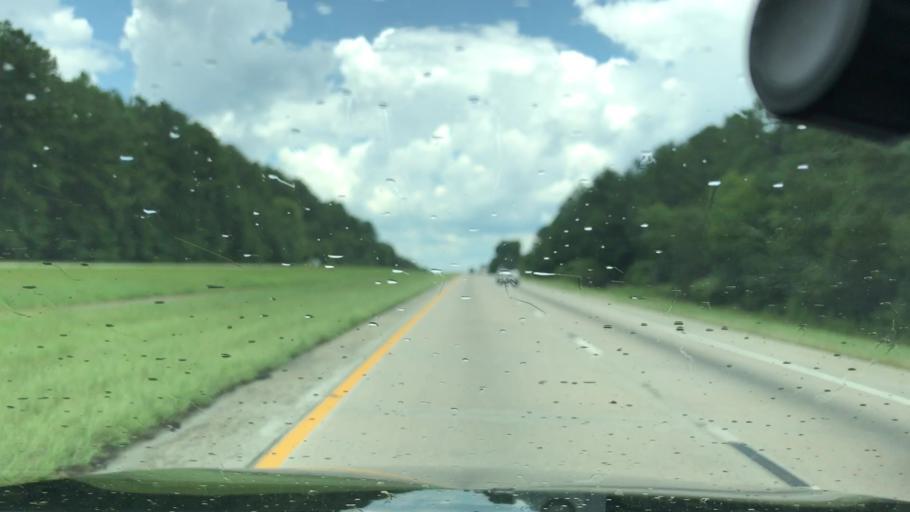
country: US
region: South Carolina
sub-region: Fairfield County
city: Winnsboro Mills
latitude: 34.3425
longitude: -81.0019
